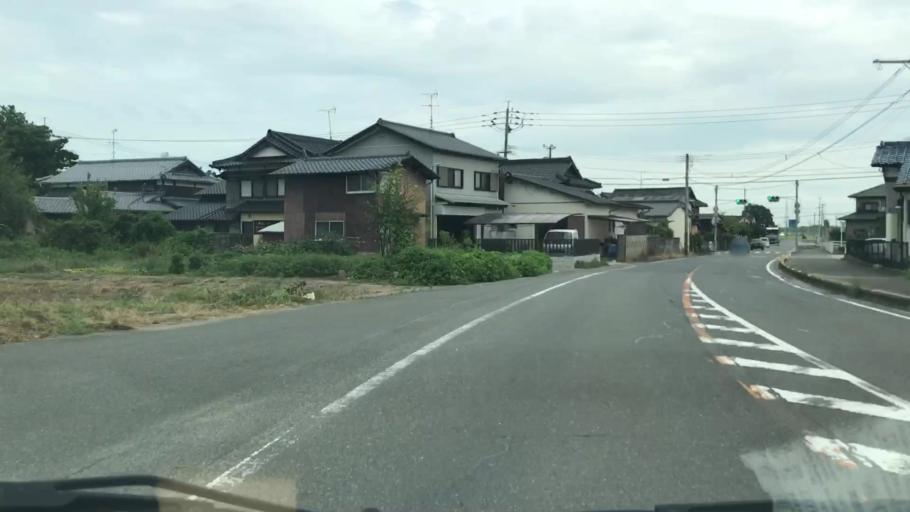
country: JP
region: Saga Prefecture
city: Saga-shi
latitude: 33.2880
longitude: 130.2499
